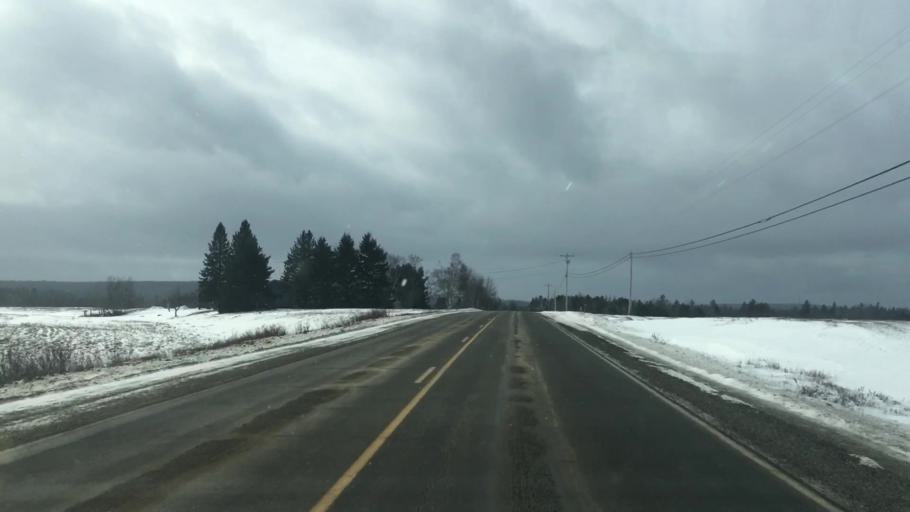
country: US
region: Maine
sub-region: Washington County
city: Calais
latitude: 45.0234
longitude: -67.3772
